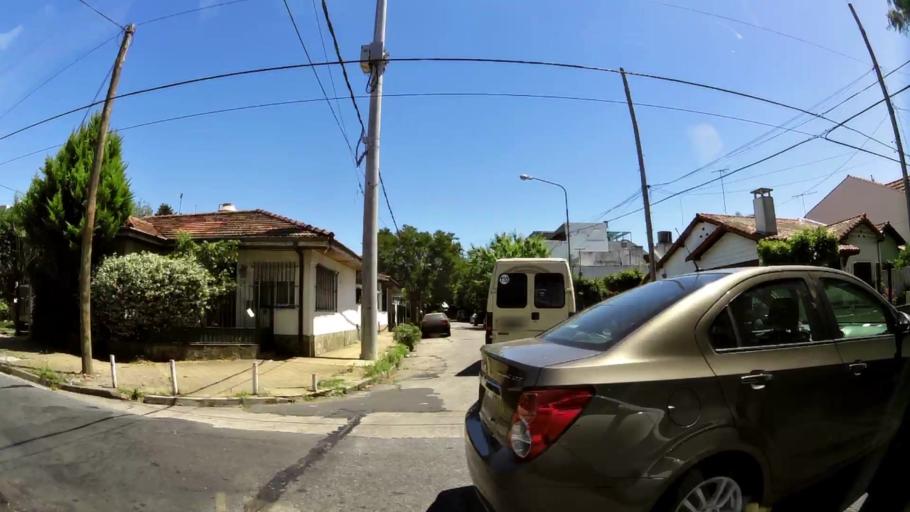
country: AR
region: Buenos Aires
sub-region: Partido de Vicente Lopez
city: Olivos
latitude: -34.5079
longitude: -58.5108
